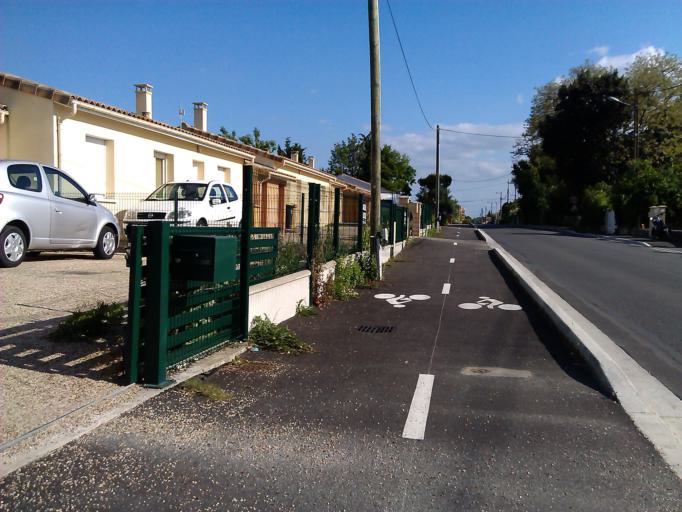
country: FR
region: Aquitaine
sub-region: Departement de la Gironde
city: Saint-Gervais
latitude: 45.0037
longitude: -0.4477
